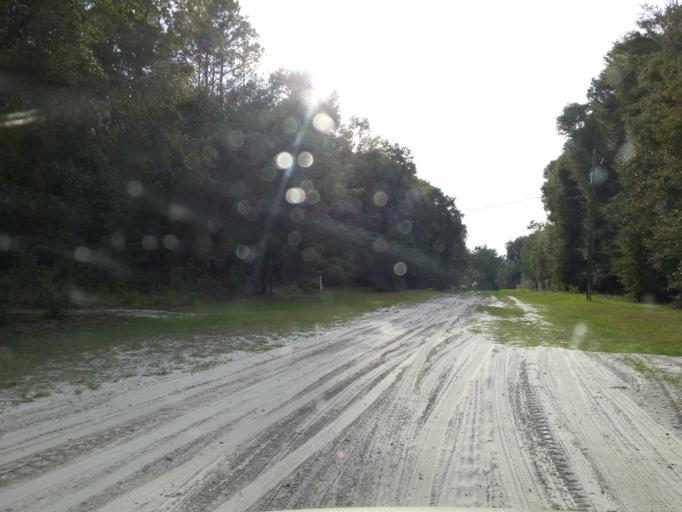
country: US
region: Florida
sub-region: Madison County
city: Madison
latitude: 30.5320
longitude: -83.2132
